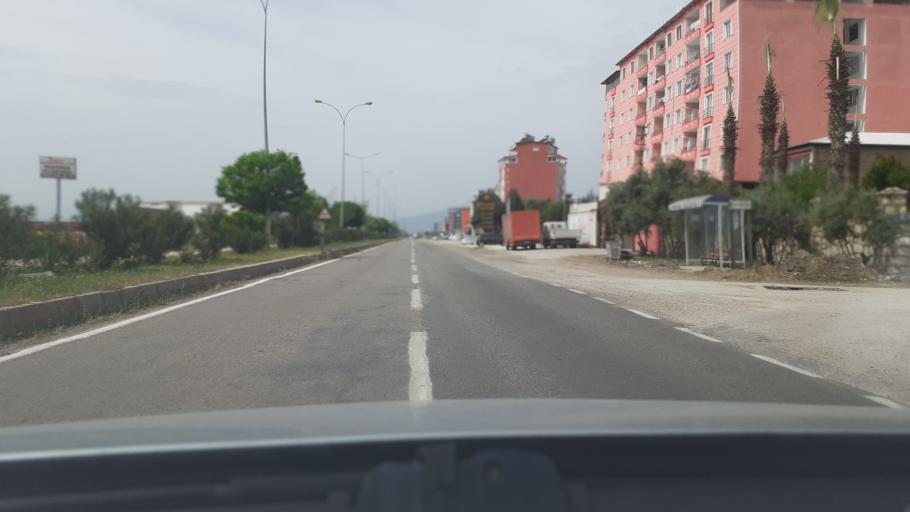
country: TR
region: Hatay
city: Kirikhan
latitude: 36.4823
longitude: 36.3594
